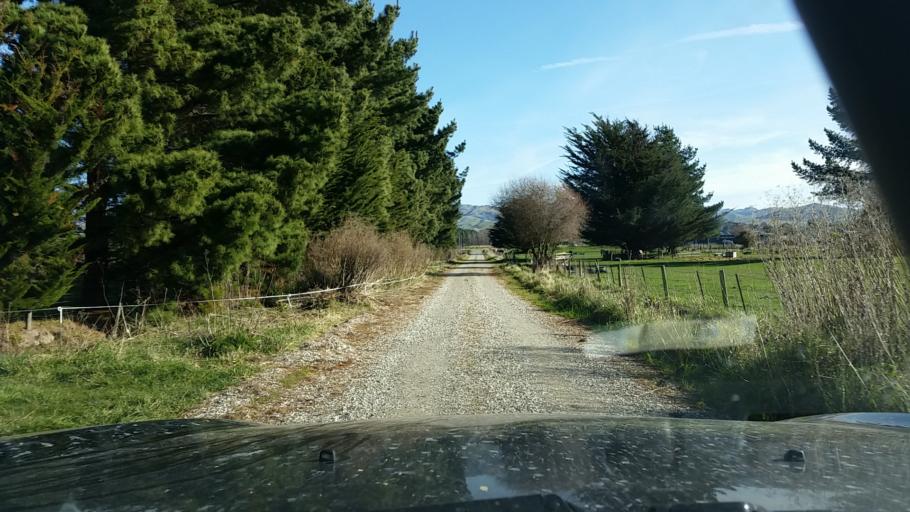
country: NZ
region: Marlborough
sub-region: Marlborough District
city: Blenheim
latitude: -41.8273
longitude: 174.1527
